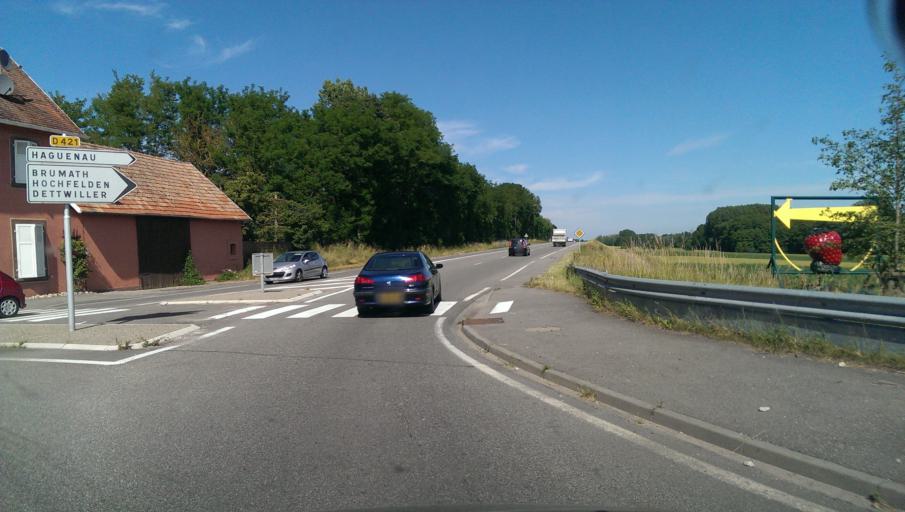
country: FR
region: Alsace
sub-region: Departement du Bas-Rhin
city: Steinbourg
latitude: 48.7455
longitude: 7.4284
